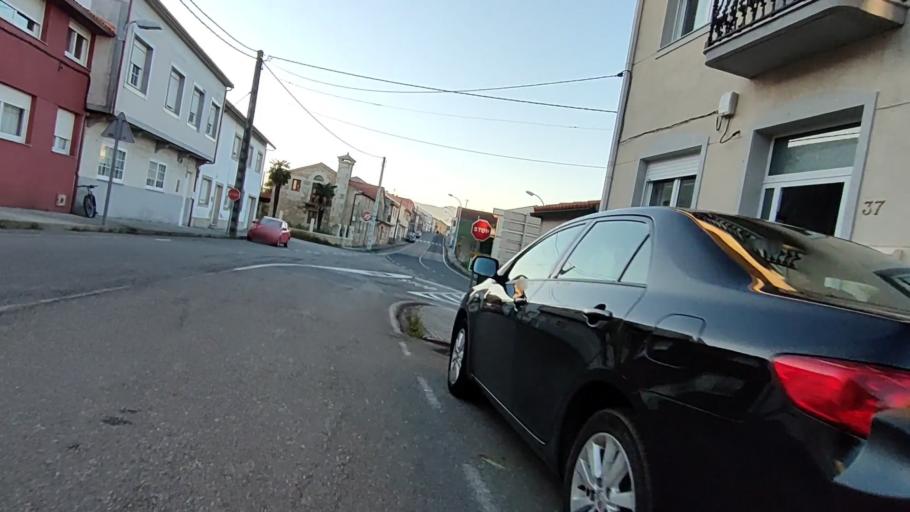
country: ES
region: Galicia
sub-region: Provincia da Coruna
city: Boiro
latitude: 42.6399
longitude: -8.8611
